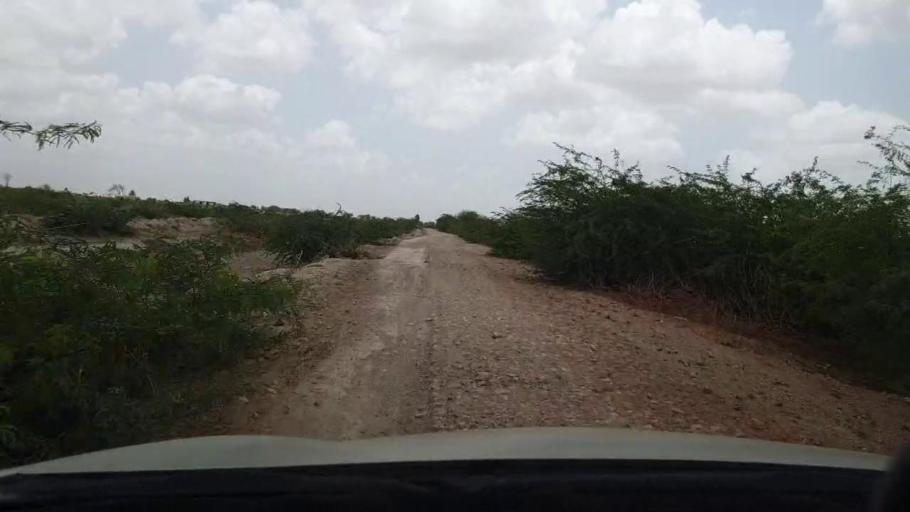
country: PK
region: Sindh
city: Kadhan
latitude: 24.3826
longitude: 68.9311
